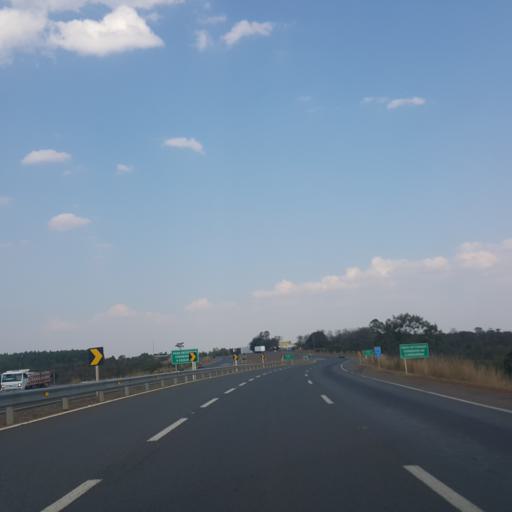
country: BR
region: Goias
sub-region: Abadiania
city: Abadiania
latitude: -16.1862
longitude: -48.6876
